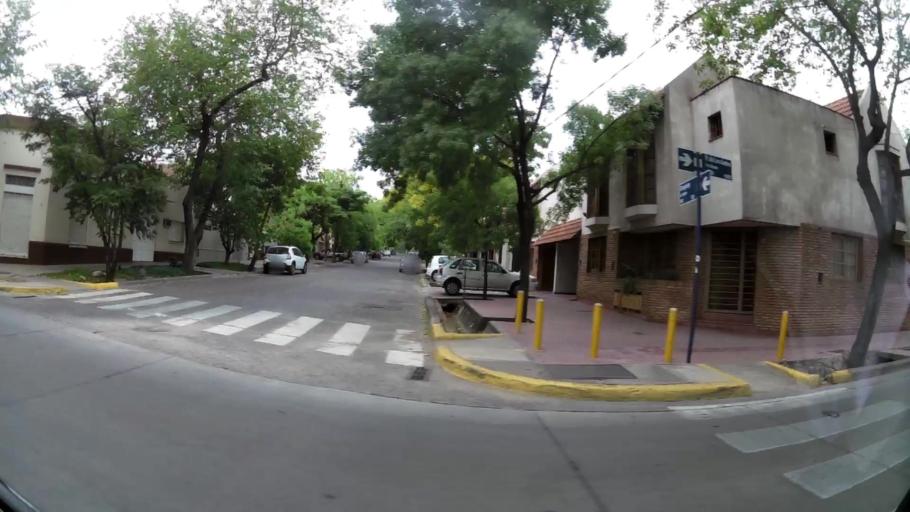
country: AR
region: Mendoza
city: Mendoza
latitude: -32.8824
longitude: -68.8586
